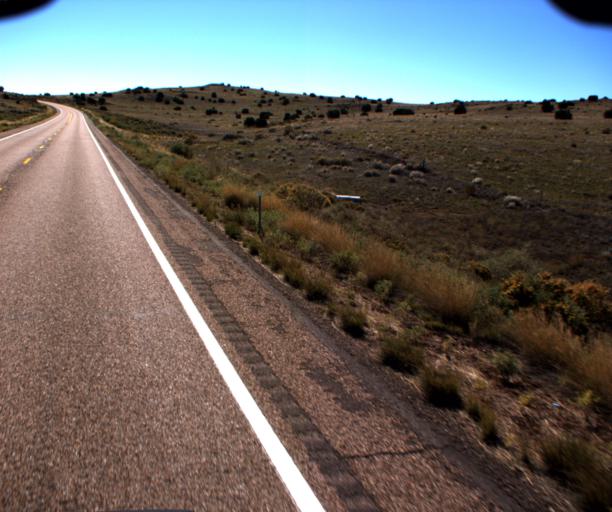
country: US
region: Arizona
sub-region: Apache County
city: Saint Johns
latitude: 34.5644
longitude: -109.5069
